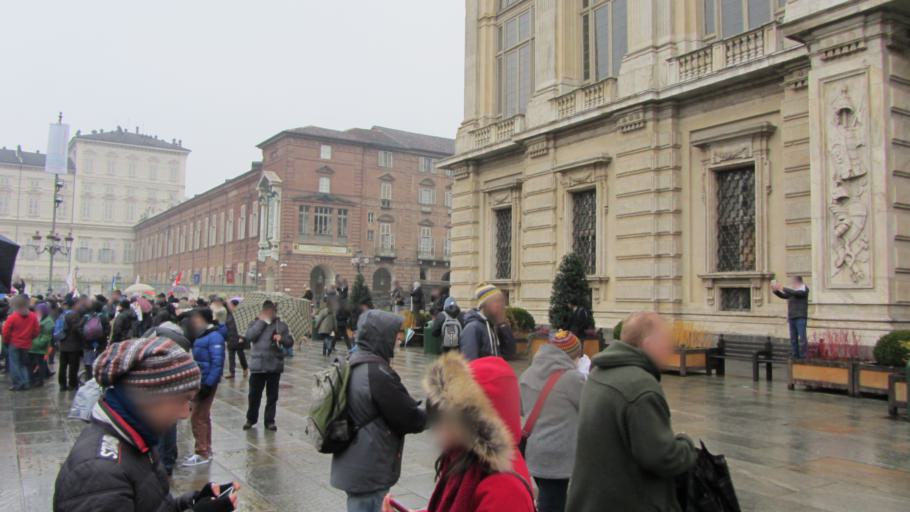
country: IT
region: Piedmont
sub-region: Provincia di Torino
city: Turin
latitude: 45.0711
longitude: 7.6852
